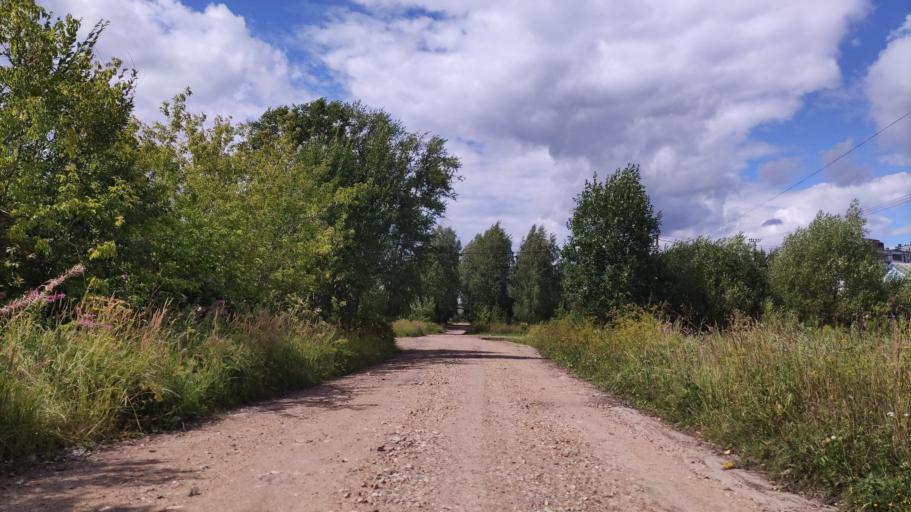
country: RU
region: Tverskaya
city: Rzhev
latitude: 56.2400
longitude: 34.3053
